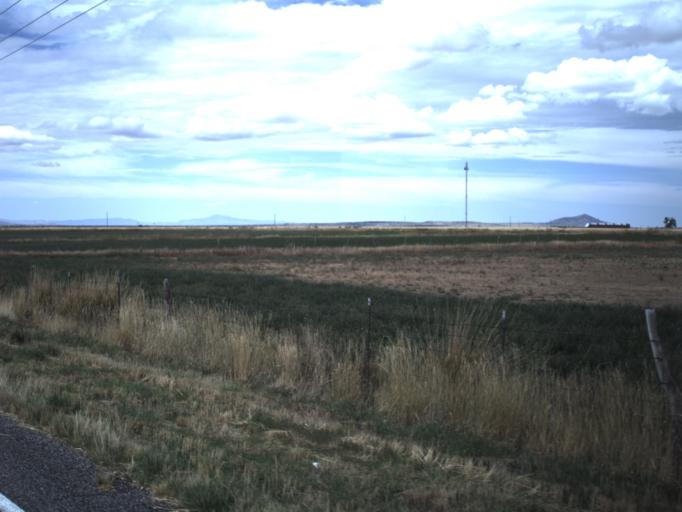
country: US
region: Utah
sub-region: Millard County
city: Fillmore
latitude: 38.9792
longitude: -112.4041
